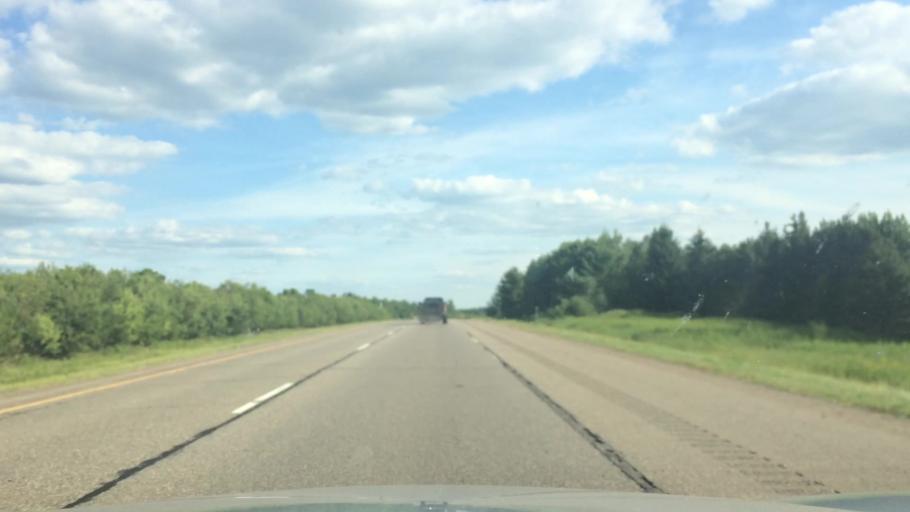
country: US
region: Wisconsin
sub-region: Lincoln County
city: Merrill
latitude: 45.1664
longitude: -89.6444
